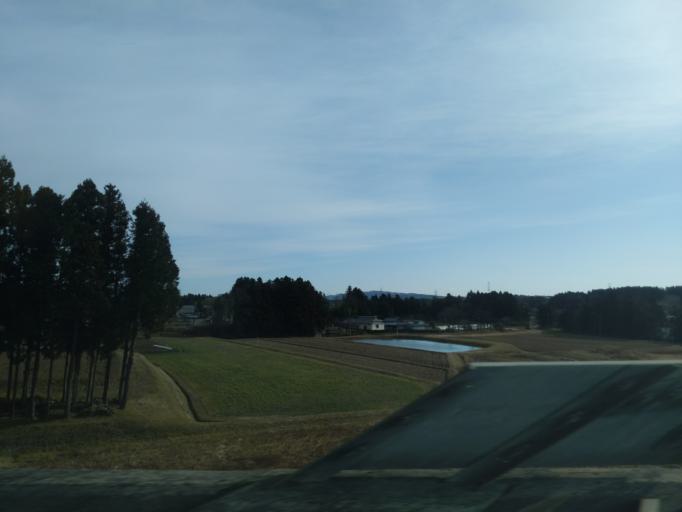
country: JP
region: Miyagi
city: Furukawa
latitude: 38.6361
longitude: 141.0078
